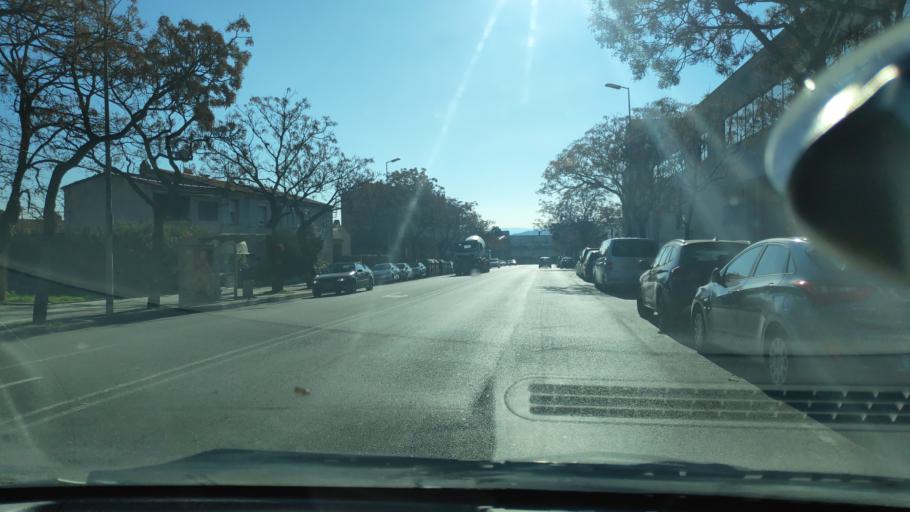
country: ES
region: Catalonia
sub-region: Provincia de Barcelona
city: Sant Quirze del Valles
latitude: 41.5436
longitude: 2.0939
